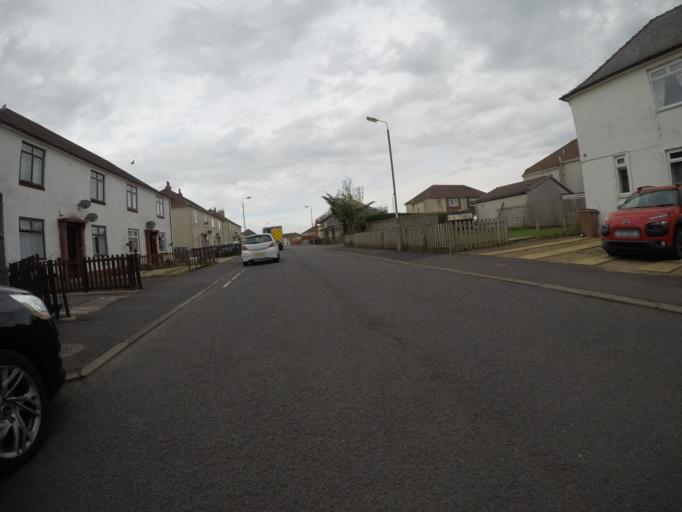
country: GB
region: Scotland
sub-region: East Ayrshire
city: Kilmaurs
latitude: 55.6395
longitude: -4.5294
